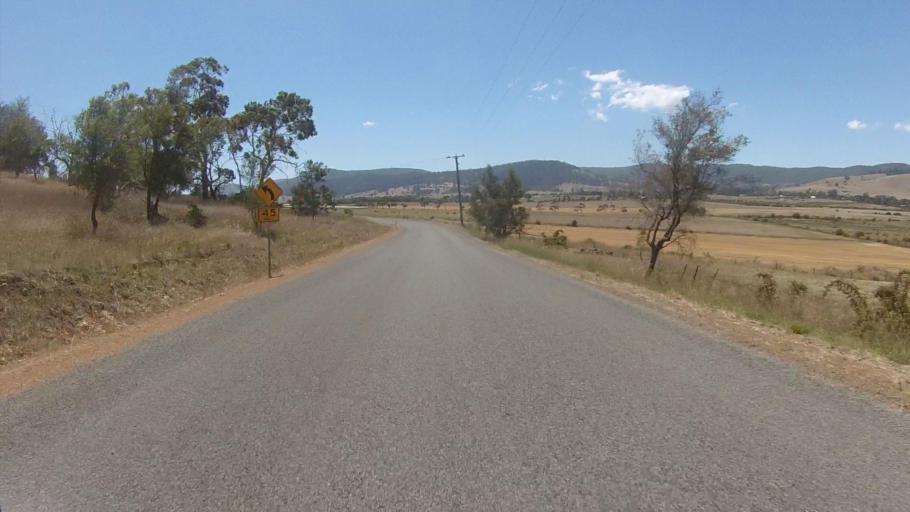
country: AU
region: Tasmania
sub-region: Sorell
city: Sorell
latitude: -42.7626
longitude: 147.5679
